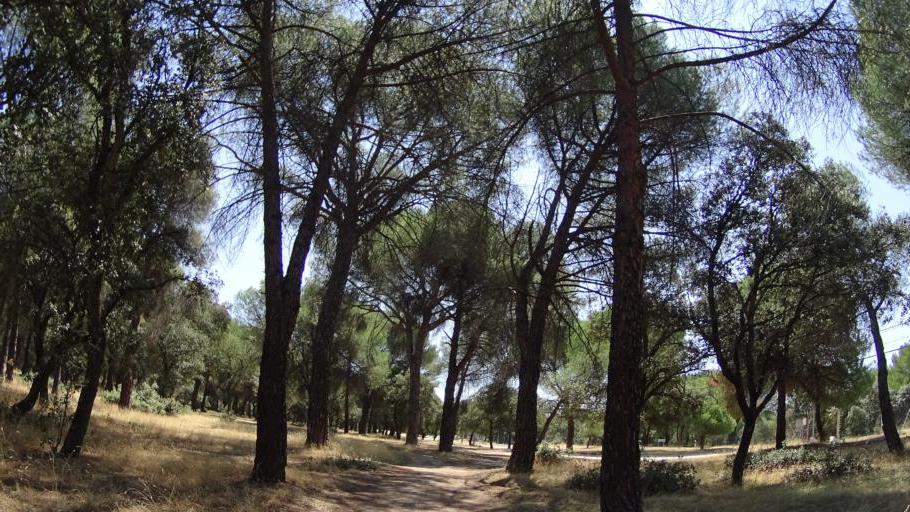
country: ES
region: Madrid
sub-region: Provincia de Madrid
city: Boadilla del Monte
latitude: 40.4352
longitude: -3.8747
